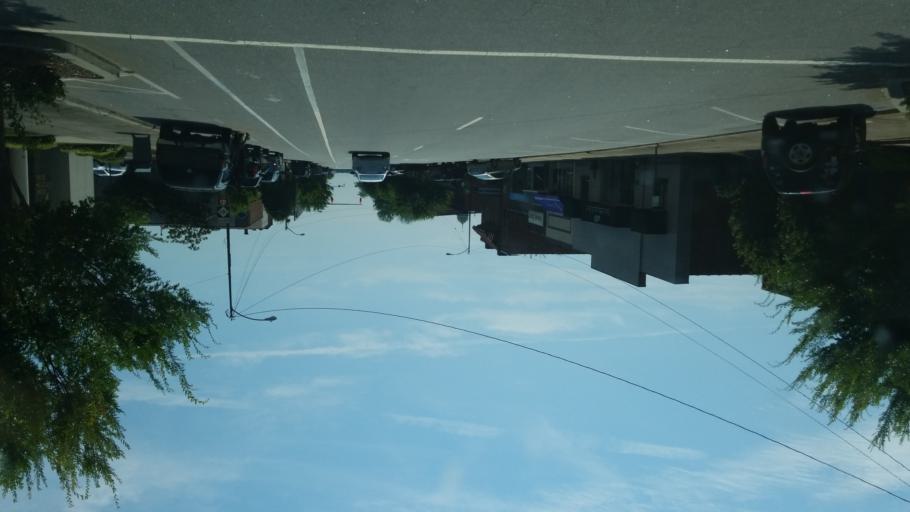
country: US
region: North Carolina
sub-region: Burke County
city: Morganton
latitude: 35.7469
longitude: -81.6901
